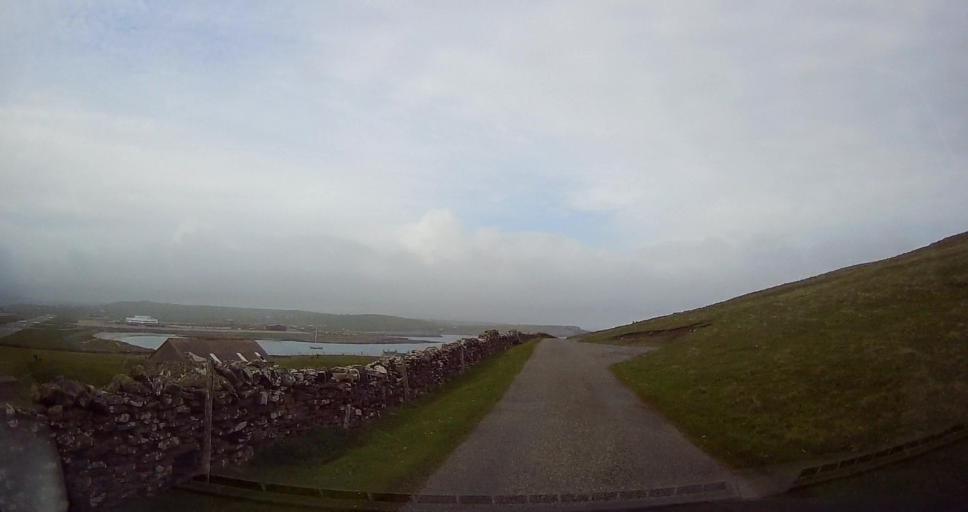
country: GB
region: Scotland
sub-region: Shetland Islands
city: Sandwick
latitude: 59.8687
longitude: -1.2793
